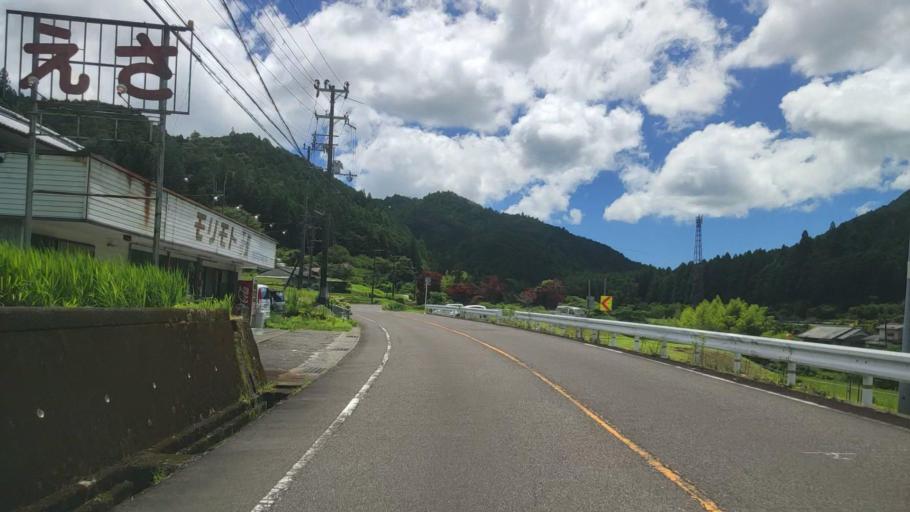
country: JP
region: Mie
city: Owase
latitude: 33.9727
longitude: 136.0590
